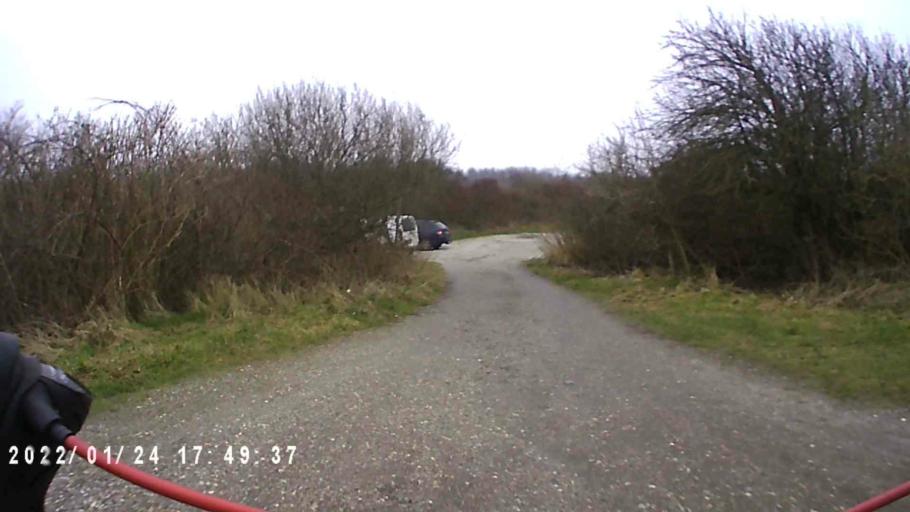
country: NL
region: Friesland
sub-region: Gemeente Schiermonnikoog
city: Schiermonnikoog
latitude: 53.4108
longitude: 6.2258
